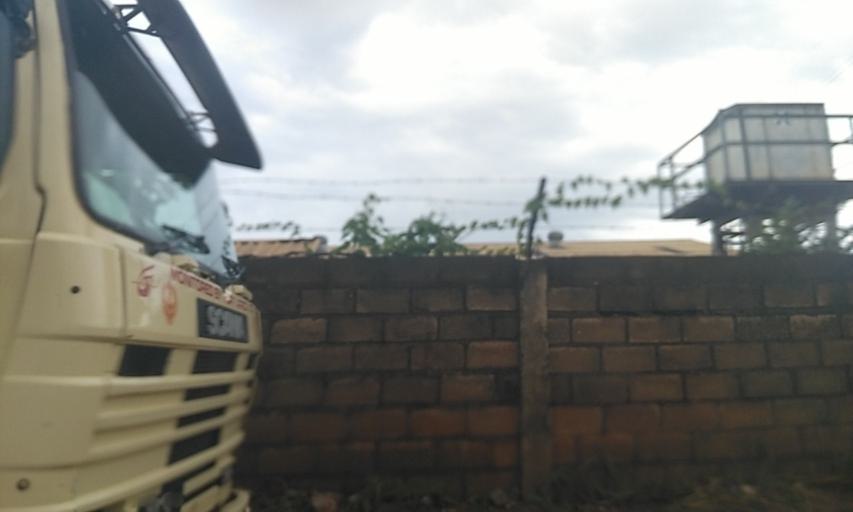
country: UG
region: Central Region
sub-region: Wakiso District
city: Bweyogerere
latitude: 0.3623
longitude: 32.6661
